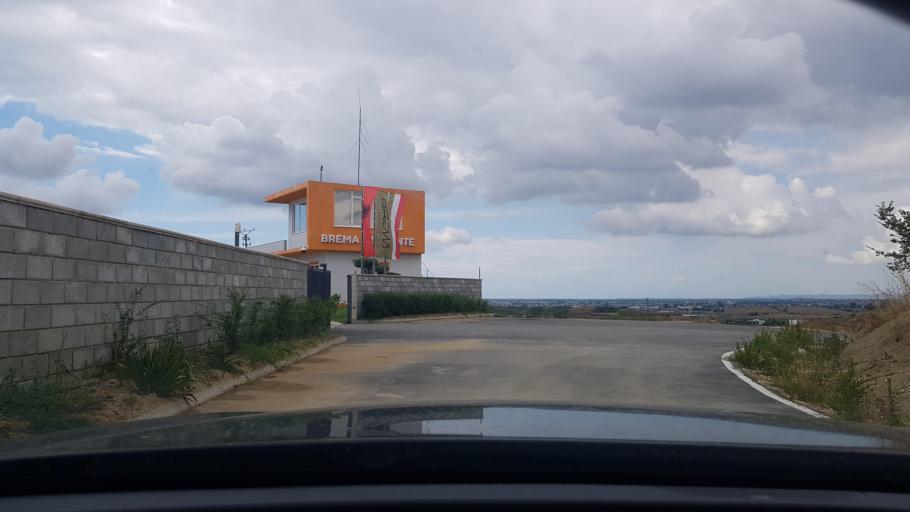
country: AL
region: Durres
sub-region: Rrethi i Durresit
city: Gjepalaj
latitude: 41.3027
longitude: 19.5523
